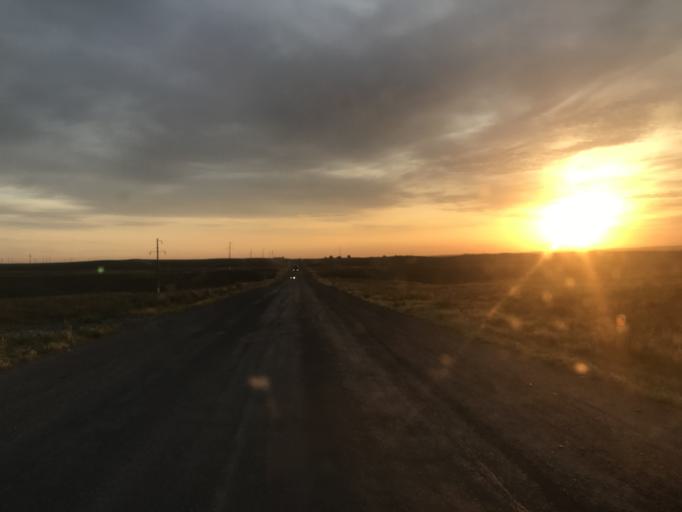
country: UZ
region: Toshkent
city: Zafar
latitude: 41.1780
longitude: 68.7637
